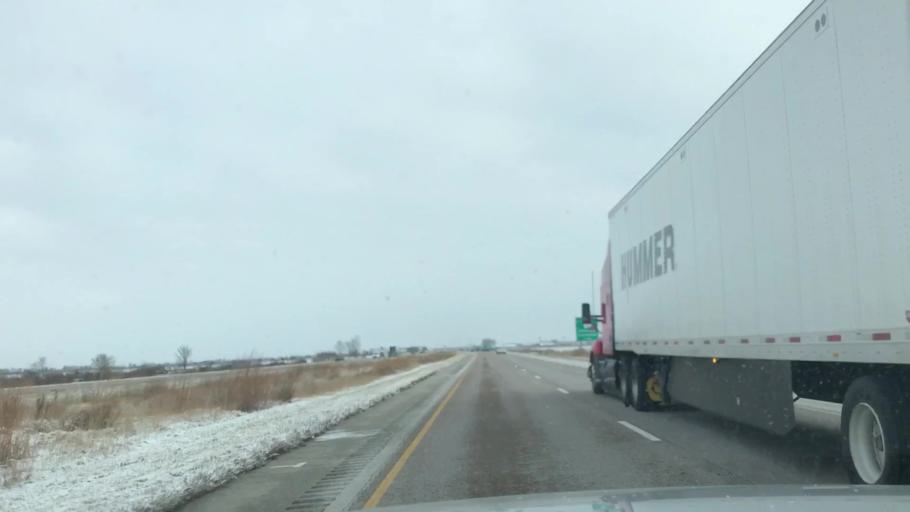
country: US
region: Illinois
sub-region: Montgomery County
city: Litchfield
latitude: 39.1570
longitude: -89.6934
